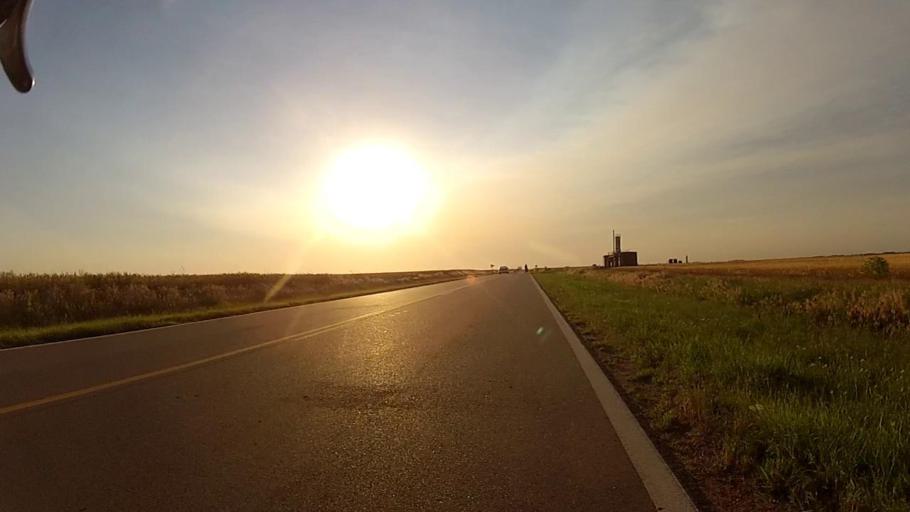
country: US
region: Kansas
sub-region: Harper County
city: Anthony
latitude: 37.1532
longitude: -97.9163
